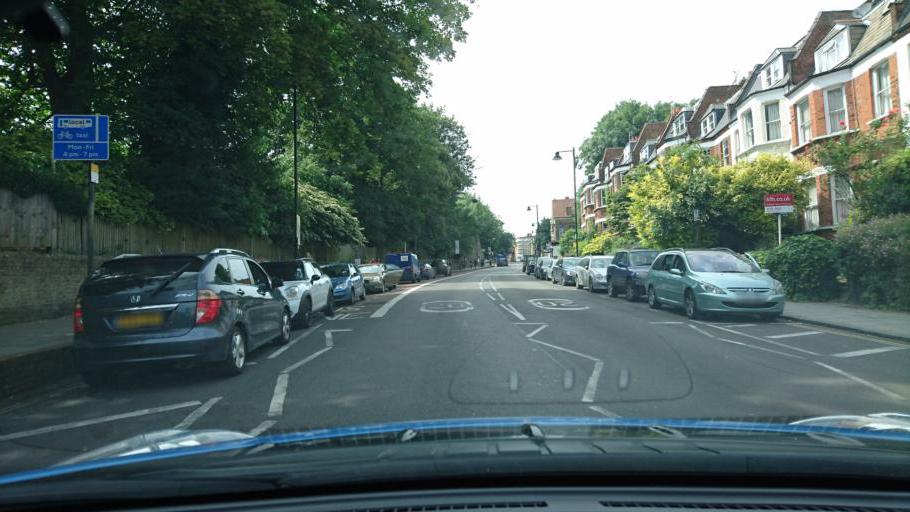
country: GB
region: England
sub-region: Greater London
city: Crouch End
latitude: 51.5683
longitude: -0.1401
